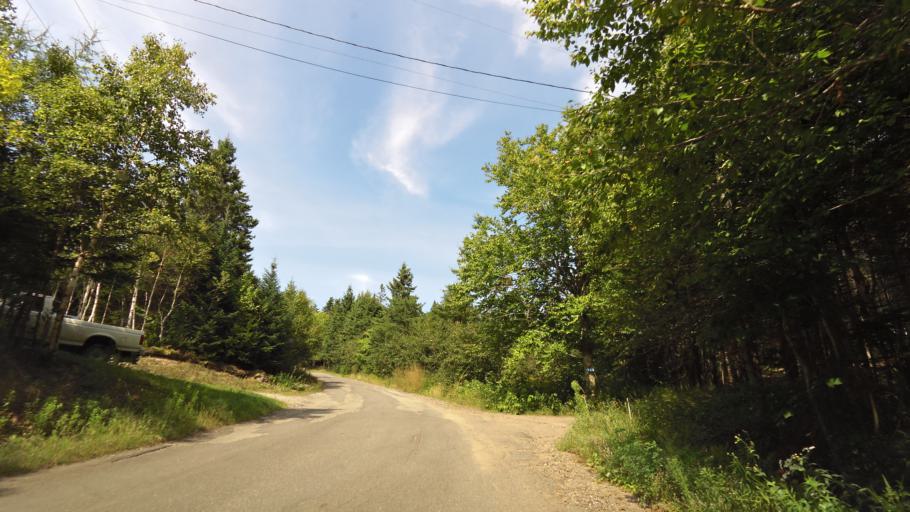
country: CA
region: New Brunswick
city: Hampton
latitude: 45.5581
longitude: -65.8427
